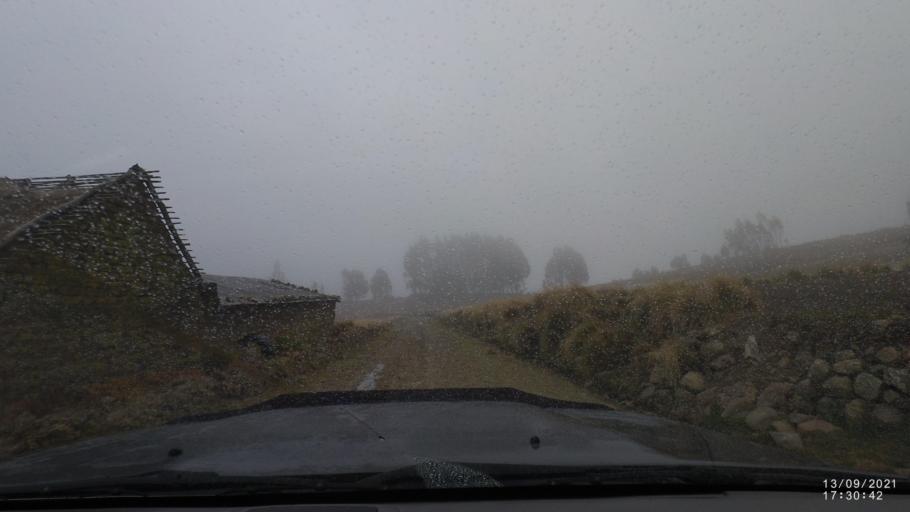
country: BO
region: Cochabamba
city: Colomi
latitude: -17.3610
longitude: -65.7879
